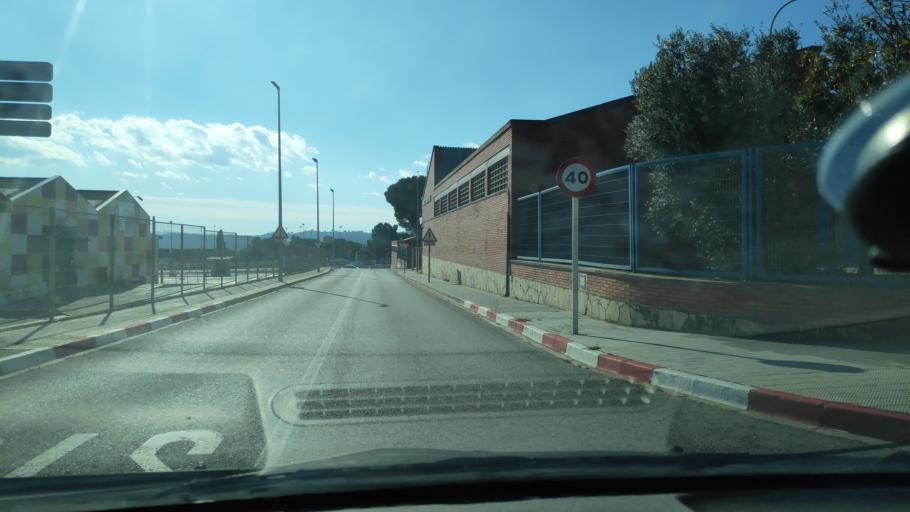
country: ES
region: Catalonia
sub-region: Provincia de Barcelona
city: Sant Quirze del Valles
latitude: 41.5547
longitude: 2.0591
